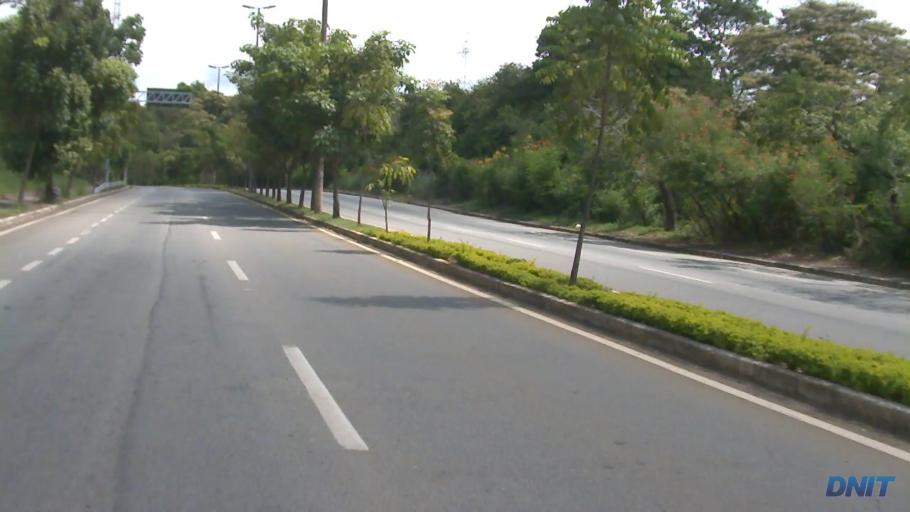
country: BR
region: Minas Gerais
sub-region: Coronel Fabriciano
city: Coronel Fabriciano
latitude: -19.5046
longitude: -42.5901
